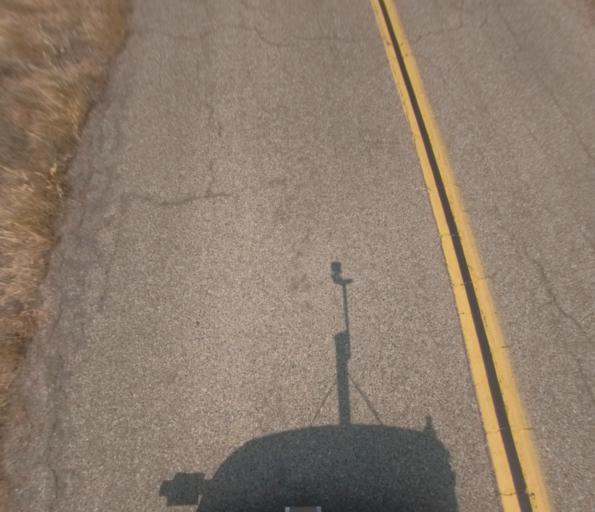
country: US
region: California
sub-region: Madera County
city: Yosemite Lakes
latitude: 37.2845
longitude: -119.8126
